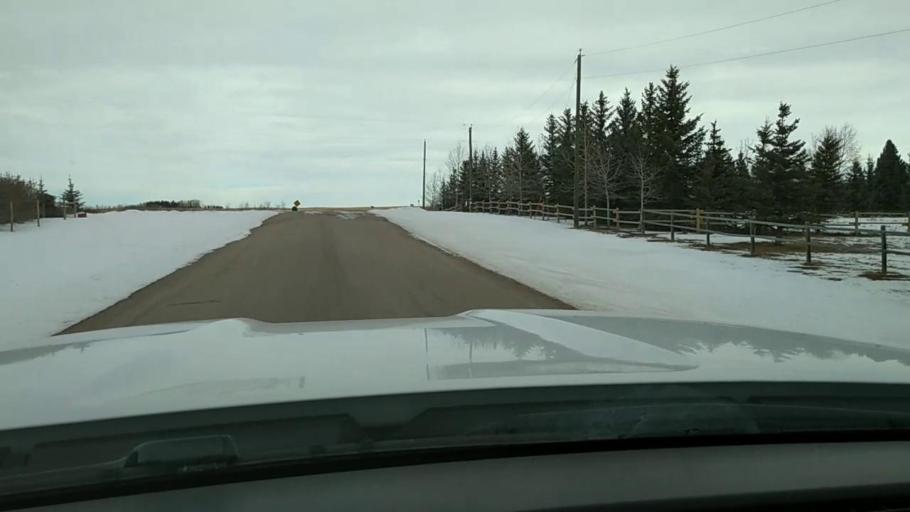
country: CA
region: Alberta
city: Cochrane
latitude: 51.2011
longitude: -114.2716
